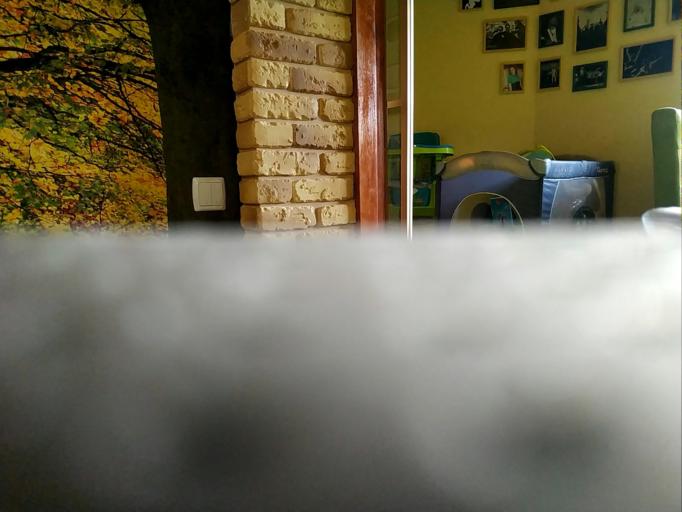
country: RU
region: Kaluga
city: Sukhinichi
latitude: 54.0618
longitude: 35.2940
